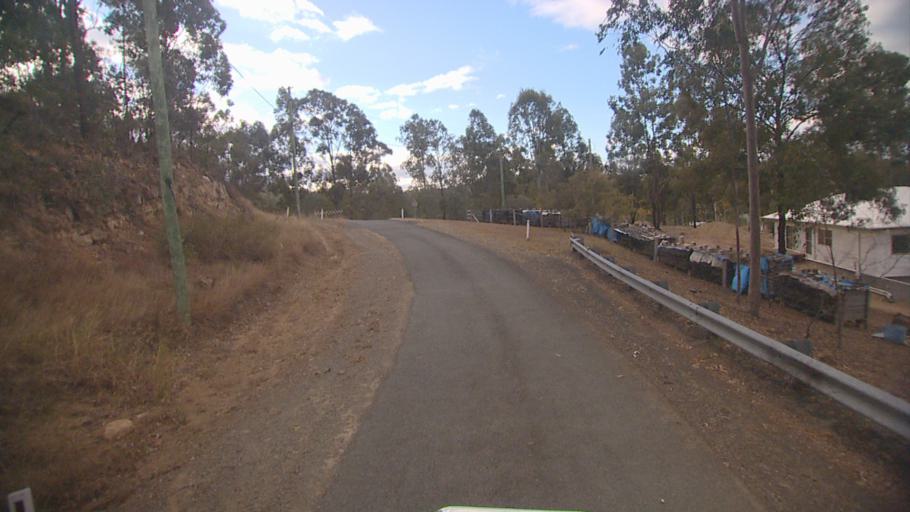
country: AU
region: Queensland
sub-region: Logan
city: Cedar Vale
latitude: -27.9334
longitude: 153.0559
